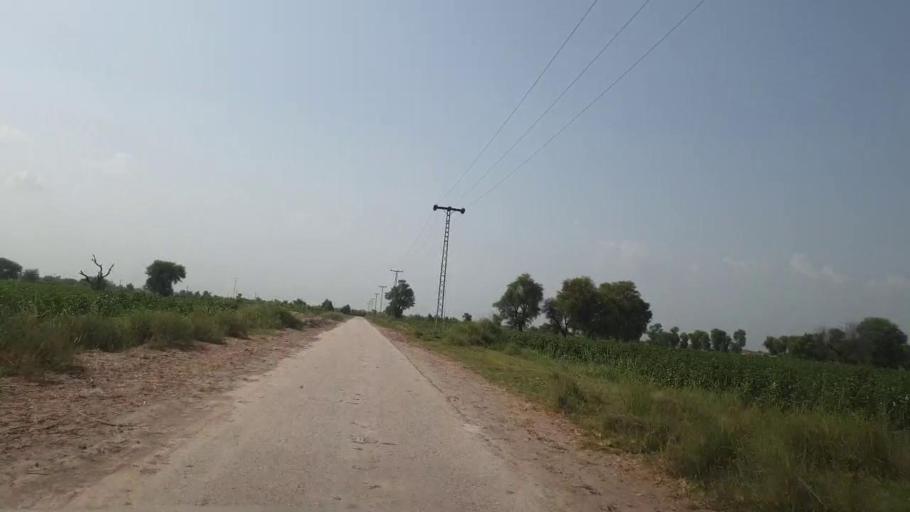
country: PK
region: Sindh
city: Pano Aqil
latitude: 27.7870
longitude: 69.1565
